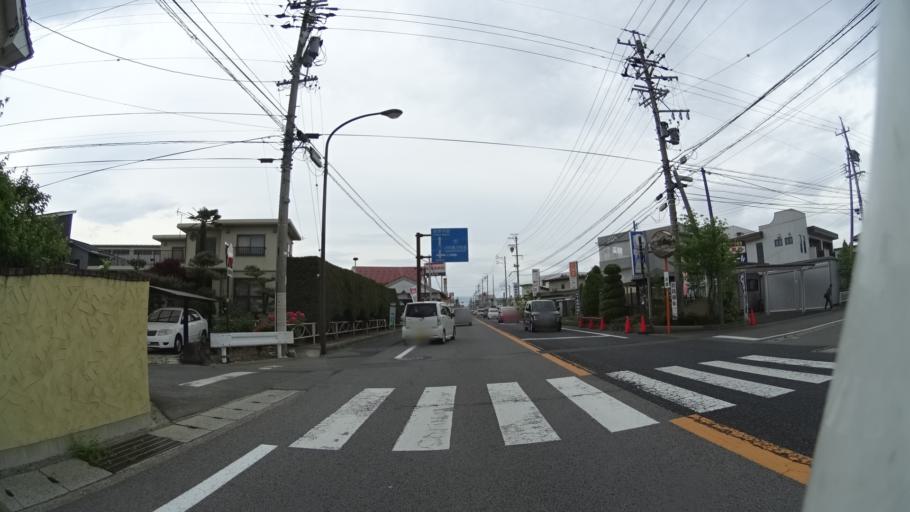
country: JP
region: Nagano
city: Nagano-shi
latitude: 36.5874
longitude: 138.1526
